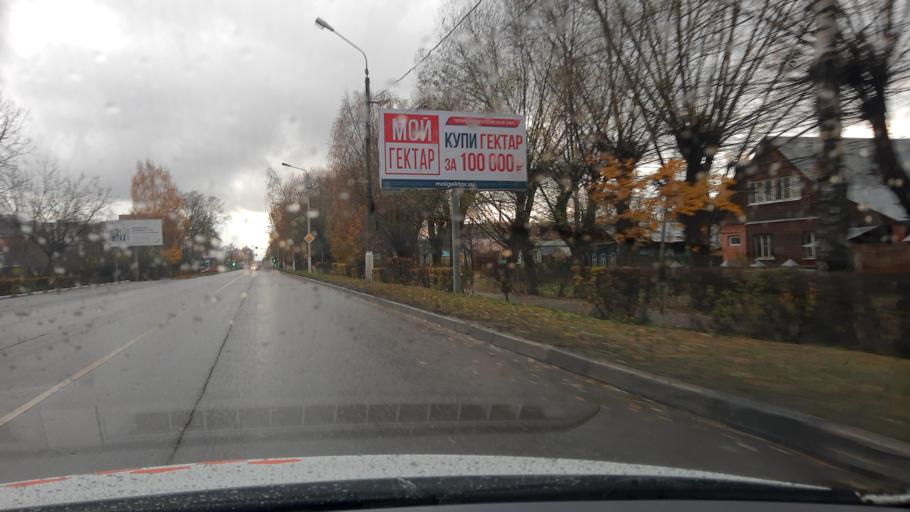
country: RU
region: Moskovskaya
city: Noginsk
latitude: 55.8474
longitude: 38.4171
